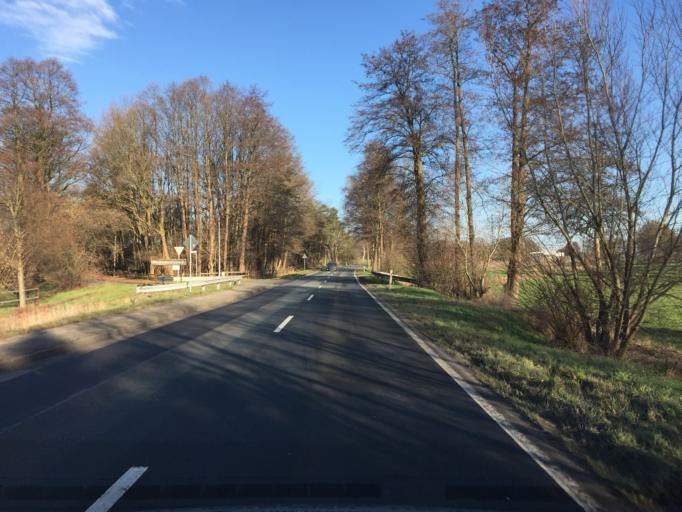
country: DE
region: Lower Saxony
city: Husum
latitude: 52.5677
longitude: 9.2547
